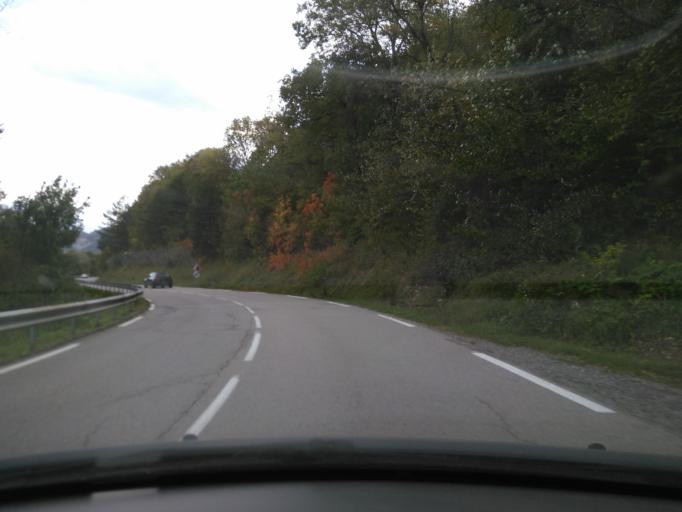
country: FR
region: Rhone-Alpes
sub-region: Departement de l'Isere
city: Sassenage
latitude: 45.2243
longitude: 5.6511
